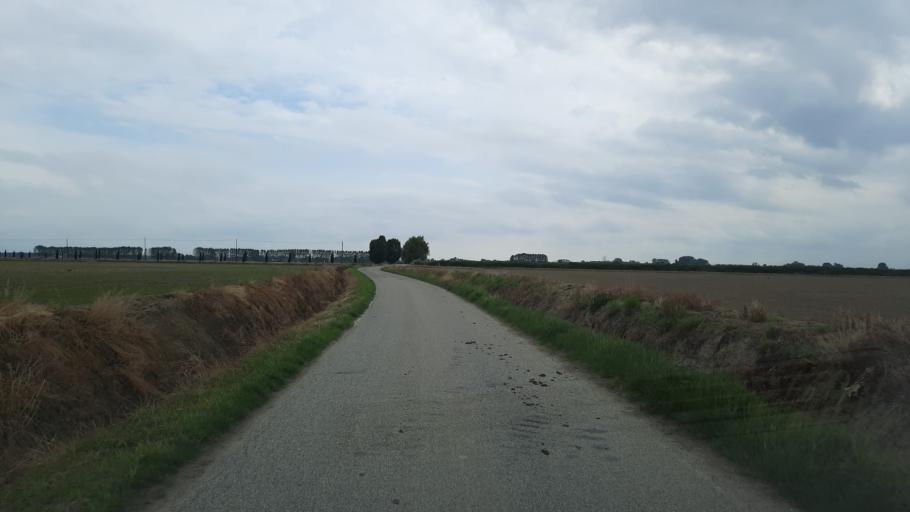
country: IT
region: Lombardy
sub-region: Provincia di Pavia
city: Castelnovetto
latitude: 45.2483
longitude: 8.6113
